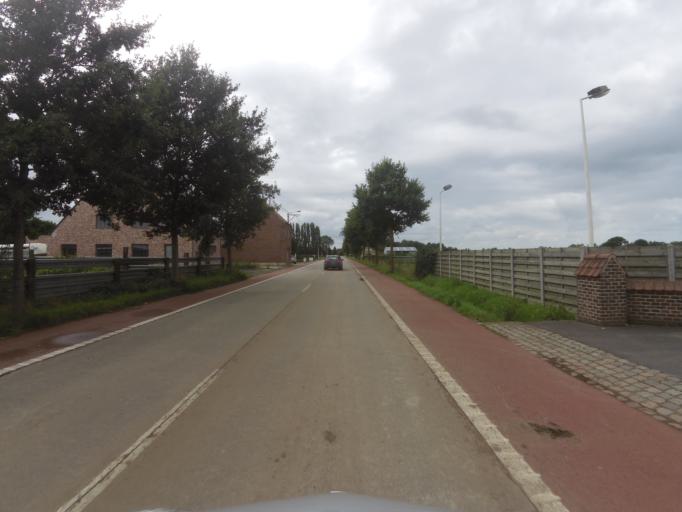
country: BE
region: Flanders
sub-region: Provincie West-Vlaanderen
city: Lichtervelde
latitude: 51.0655
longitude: 3.1455
